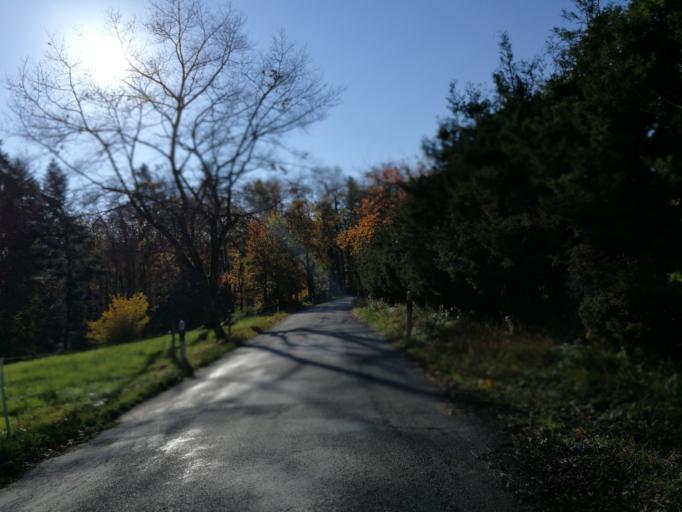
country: CH
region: Zurich
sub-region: Bezirk Uster
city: Egg
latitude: 47.3031
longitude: 8.7055
